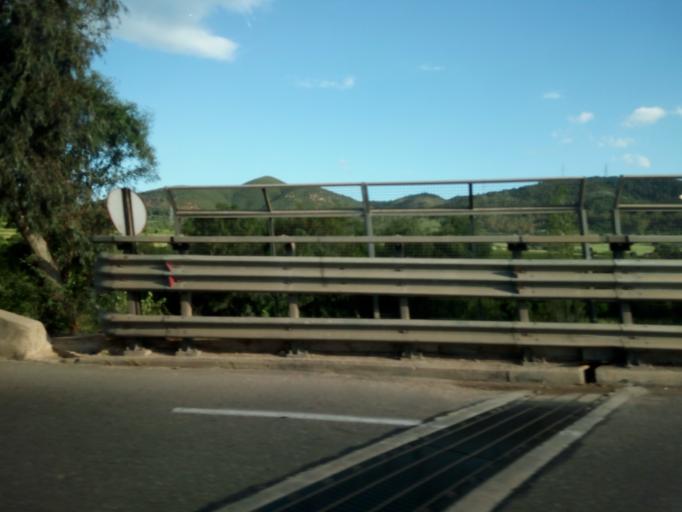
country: DZ
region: Tipaza
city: El Affroun
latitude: 36.4470
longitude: 2.5942
